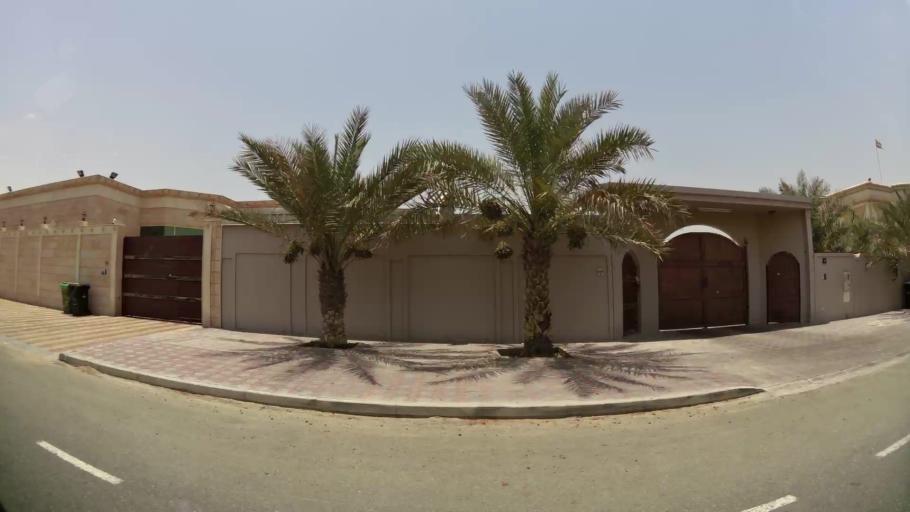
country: AE
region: Ash Shariqah
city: Sharjah
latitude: 25.2057
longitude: 55.3913
